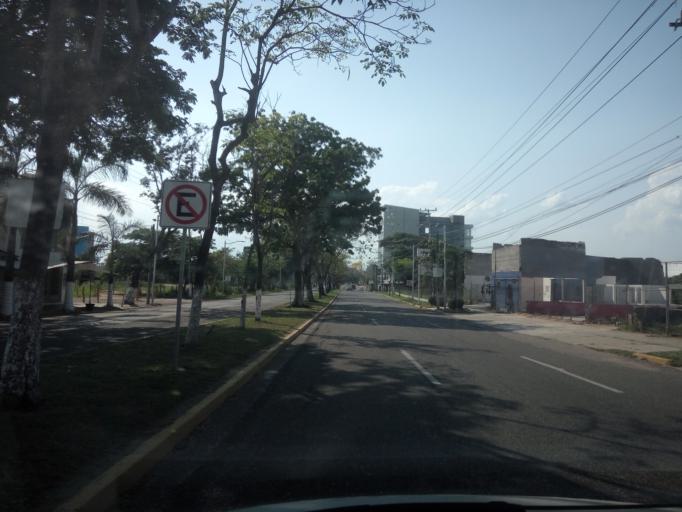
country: MX
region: Tabasco
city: Villahermosa
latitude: 17.9945
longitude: -92.9476
